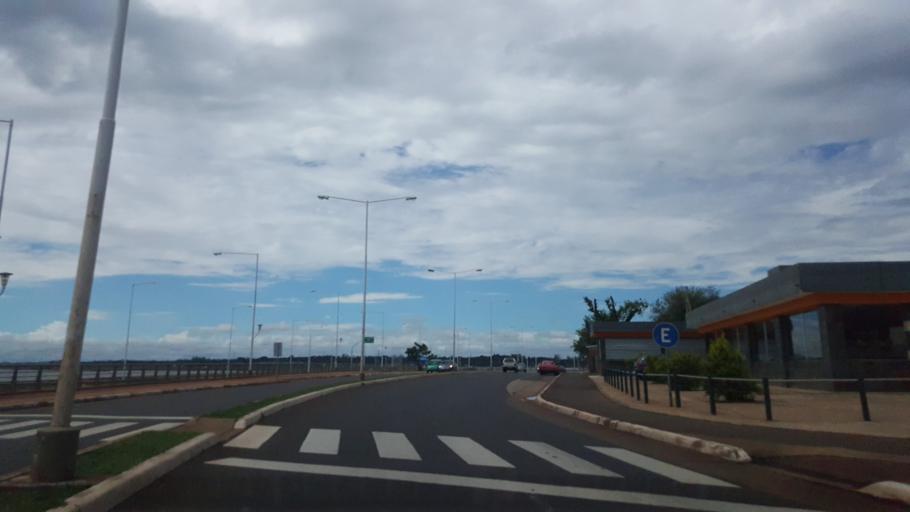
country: AR
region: Misiones
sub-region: Departamento de Capital
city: Posadas
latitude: -27.4010
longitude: -55.8923
